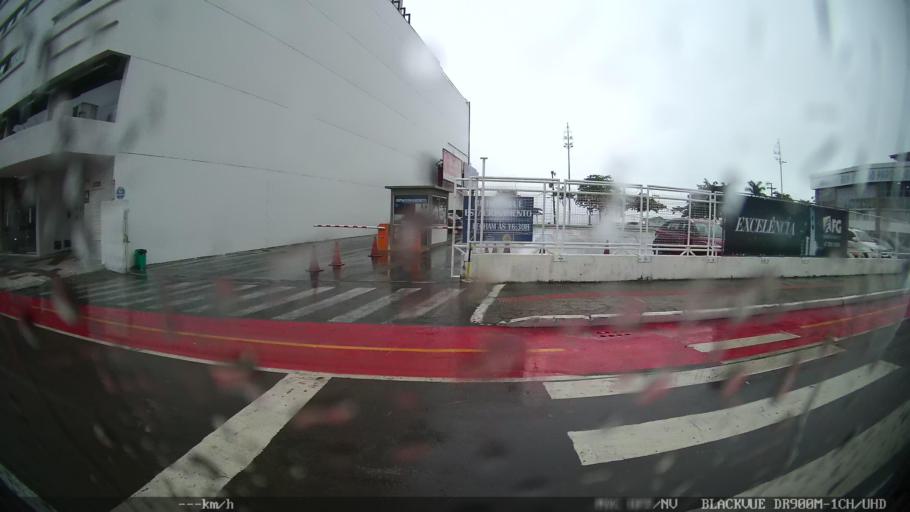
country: BR
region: Santa Catarina
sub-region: Balneario Camboriu
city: Balneario Camboriu
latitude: -27.0058
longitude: -48.6038
